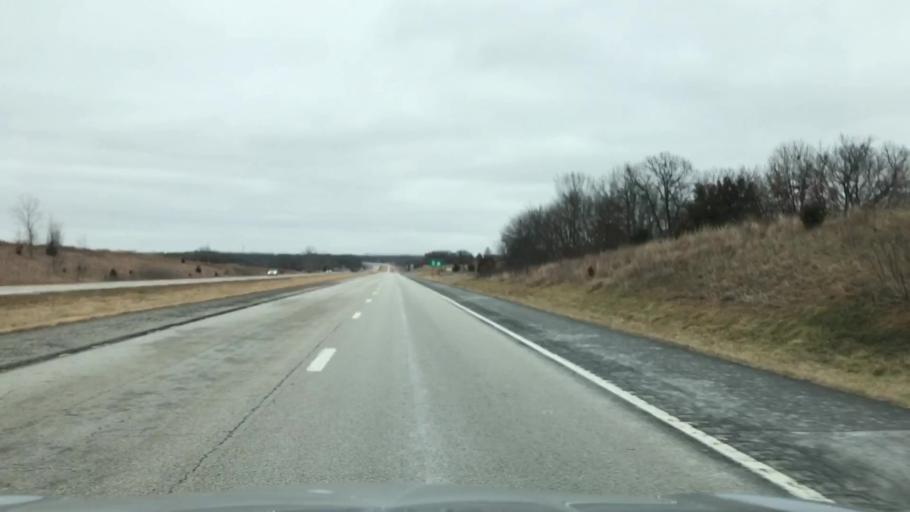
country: US
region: Missouri
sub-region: Caldwell County
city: Hamilton
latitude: 39.7447
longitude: -94.0440
